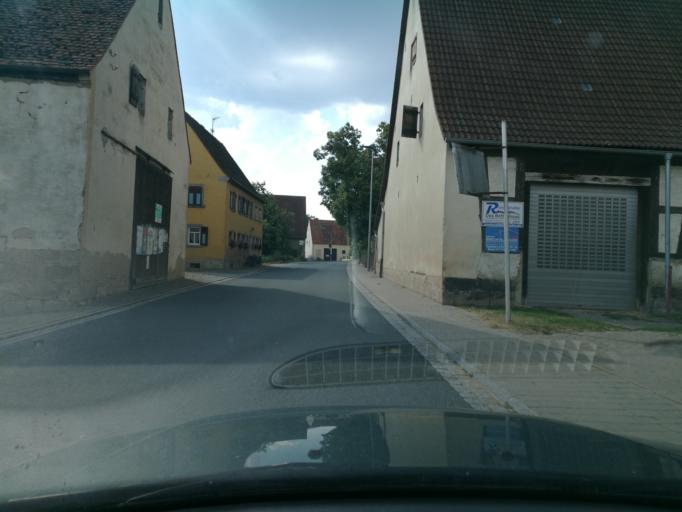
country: DE
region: Bavaria
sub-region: Regierungsbezirk Mittelfranken
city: Grosshabersdorf
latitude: 49.4190
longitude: 10.7379
